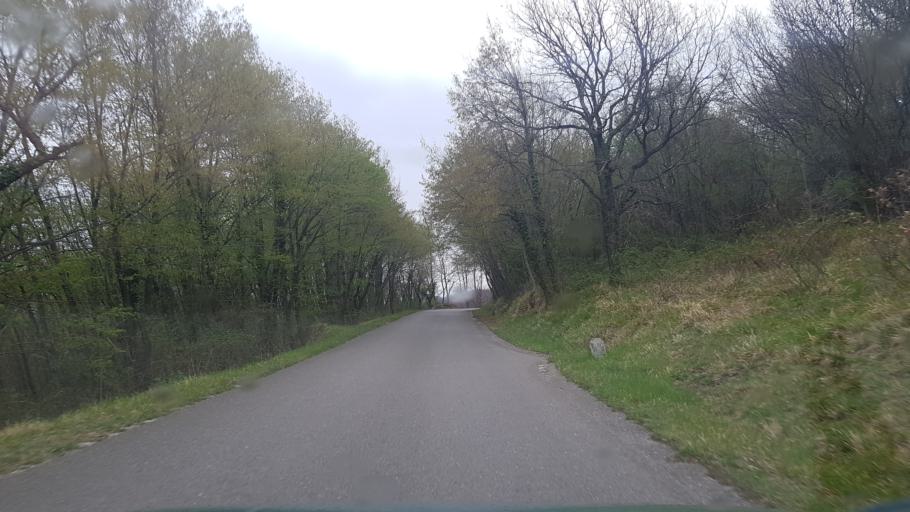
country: SI
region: Kanal
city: Deskle
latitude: 46.0428
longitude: 13.5634
